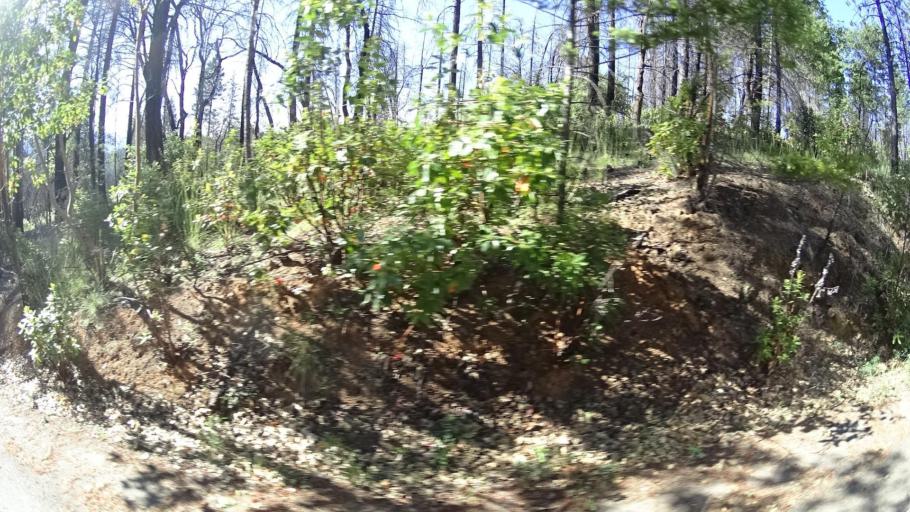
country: US
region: California
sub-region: Lake County
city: Upper Lake
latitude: 39.3978
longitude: -122.9663
